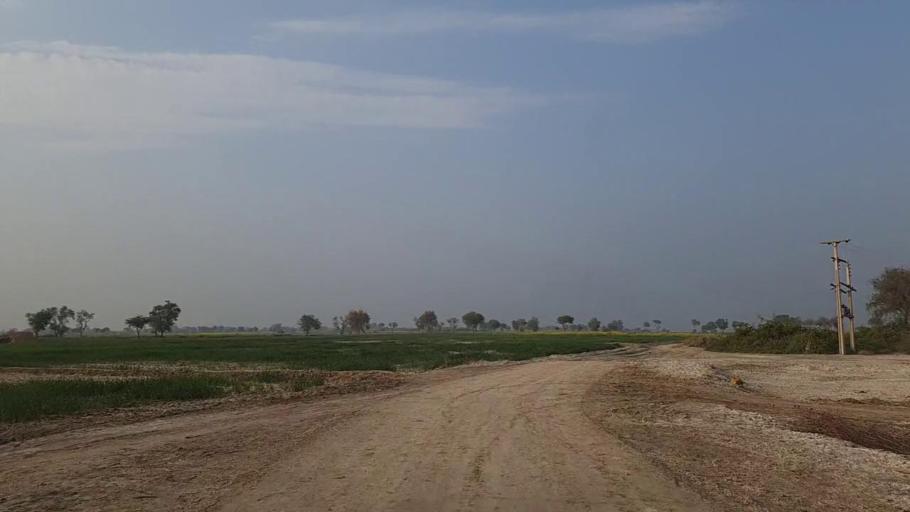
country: PK
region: Sindh
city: Jam Sahib
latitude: 26.3073
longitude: 68.5168
